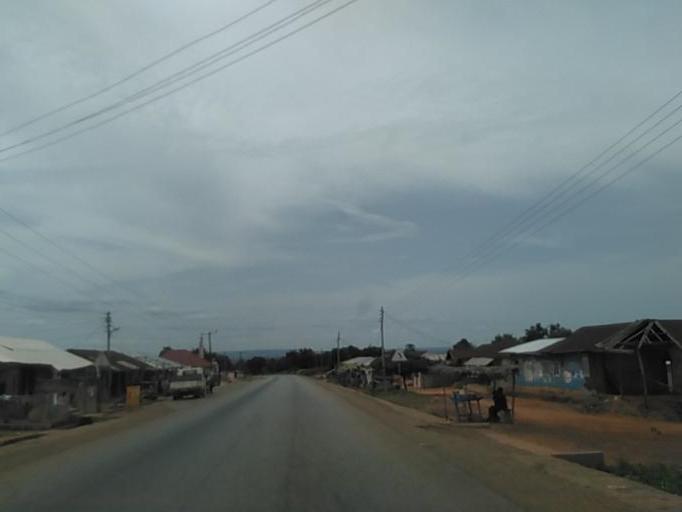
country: GH
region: Ashanti
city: Mampong
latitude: 7.1503
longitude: -1.3953
